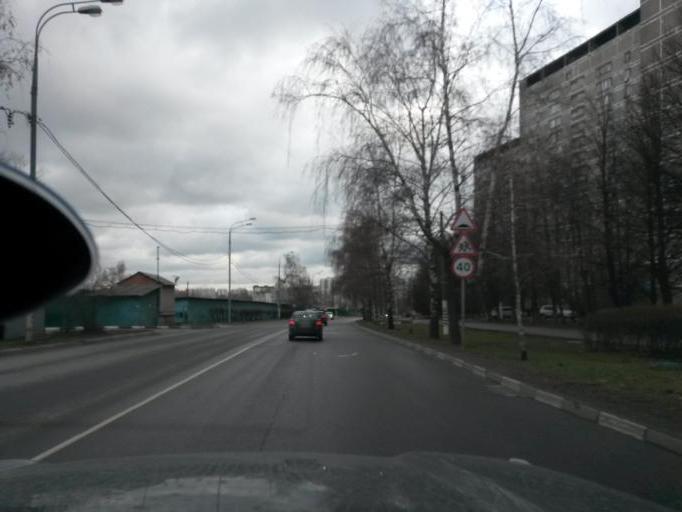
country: RU
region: Moscow
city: Orekhovo-Borisovo
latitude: 55.6229
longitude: 37.7308
